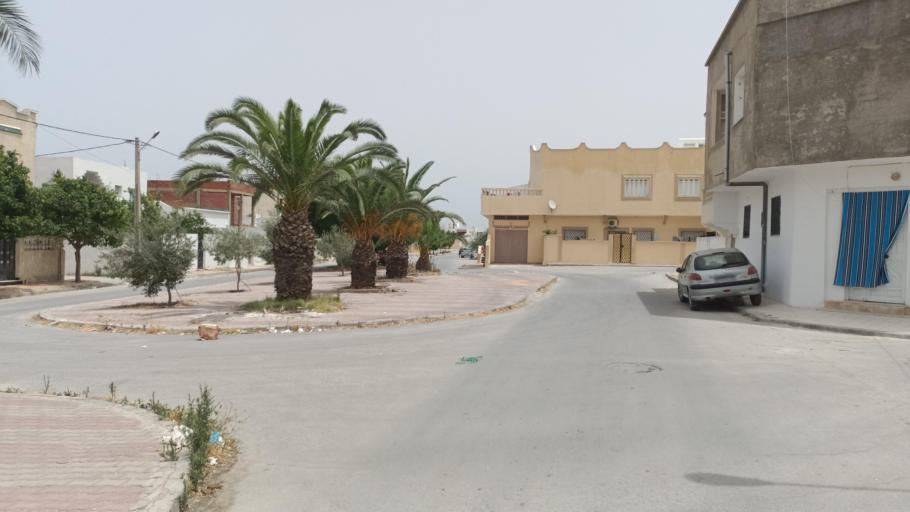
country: TN
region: Nabul
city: Manzil Bu Zalafah
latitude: 36.7018
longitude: 10.4909
